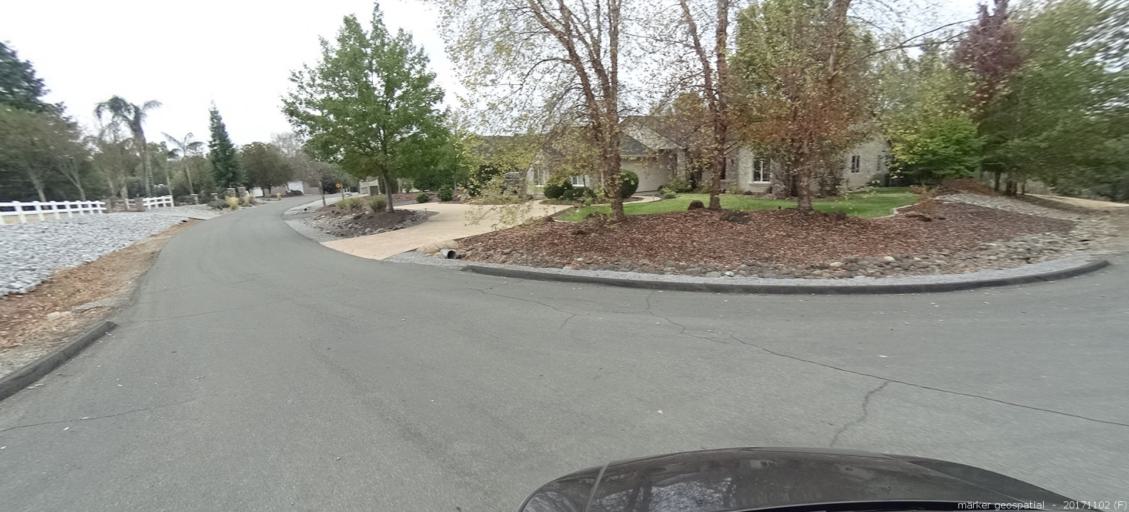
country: US
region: California
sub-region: Shasta County
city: Shasta Lake
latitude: 40.6528
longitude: -122.3232
